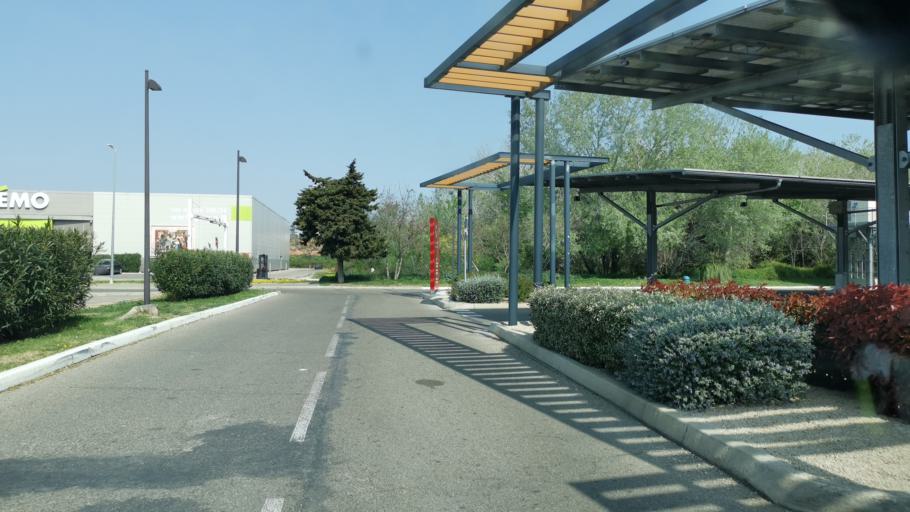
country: FR
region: Provence-Alpes-Cote d'Azur
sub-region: Departement des Bouches-du-Rhone
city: Arles
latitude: 43.6671
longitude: 4.6373
